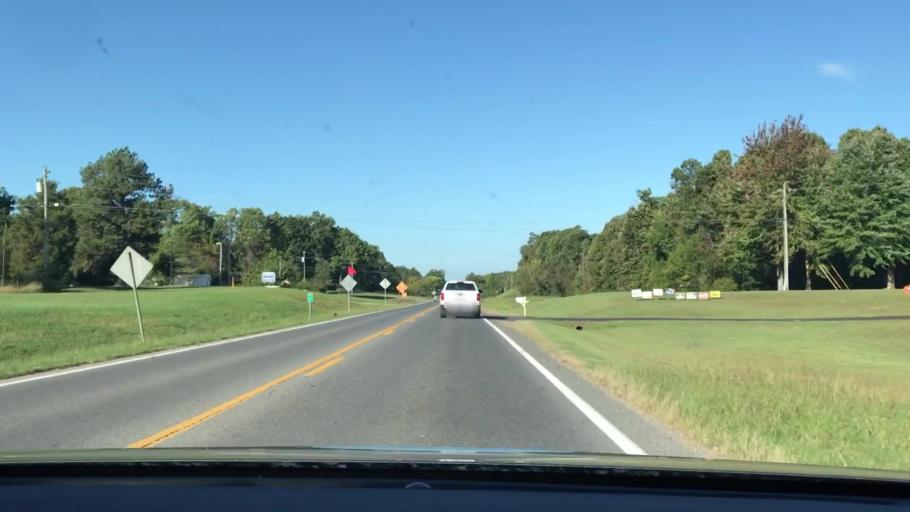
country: US
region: Kentucky
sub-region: Marshall County
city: Calvert City
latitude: 37.0042
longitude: -88.3573
